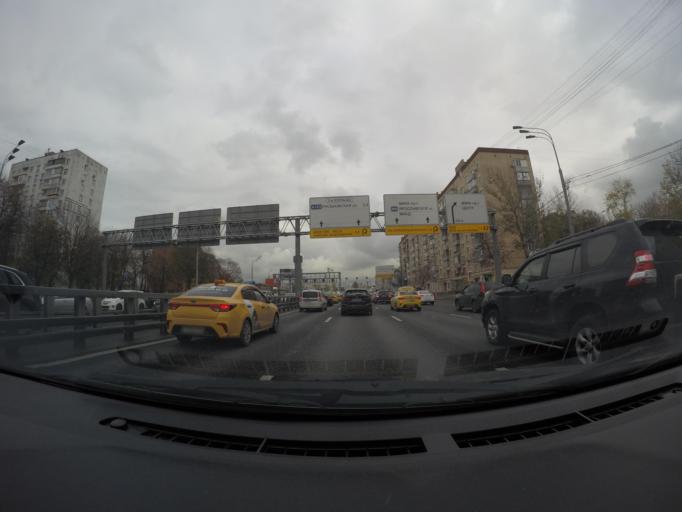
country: RU
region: Moscow
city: Mar'ina Roshcha
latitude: 55.7926
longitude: 37.6260
